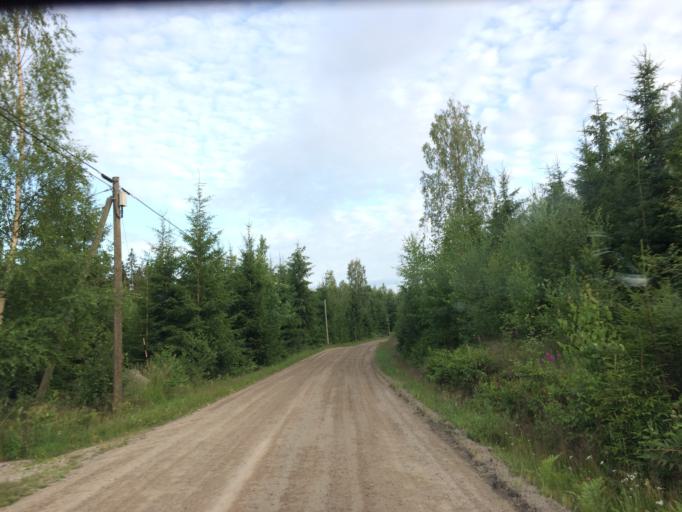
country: FI
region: Haeme
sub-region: Haemeenlinna
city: Janakkala
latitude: 60.8862
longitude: 24.6101
